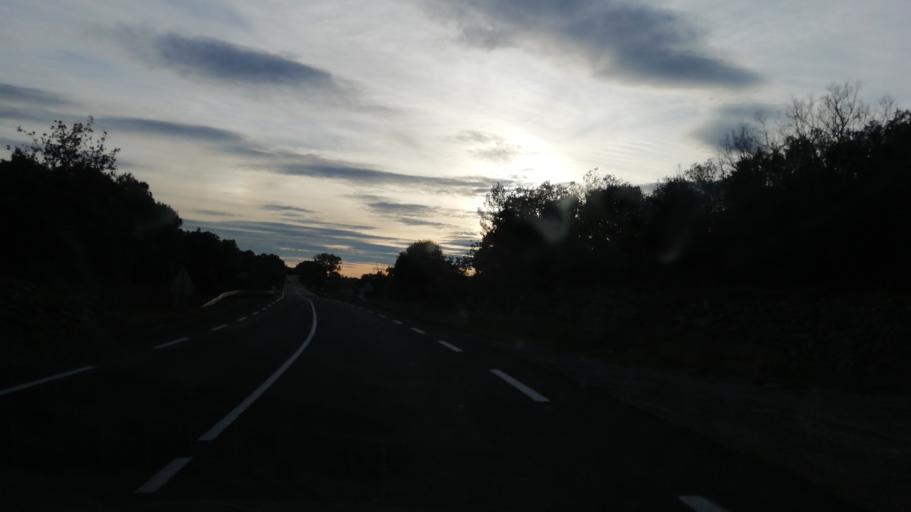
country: FR
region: Languedoc-Roussillon
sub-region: Departement de l'Herault
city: Claret
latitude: 43.8558
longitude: 3.9299
